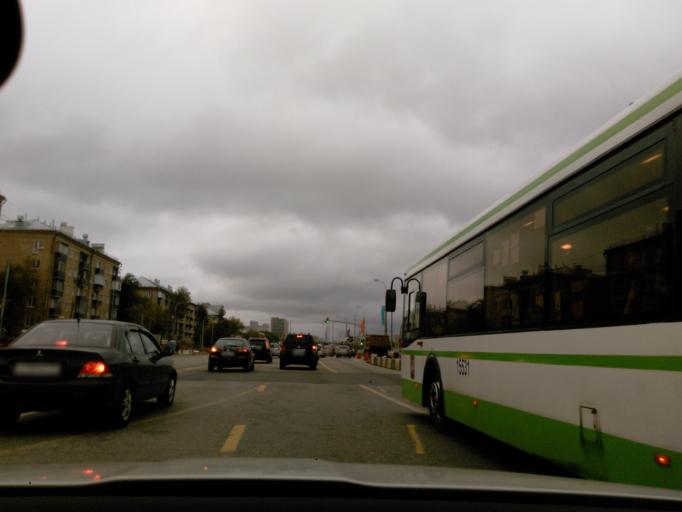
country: RU
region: Moscow
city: Strogino
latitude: 55.8265
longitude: 37.4250
